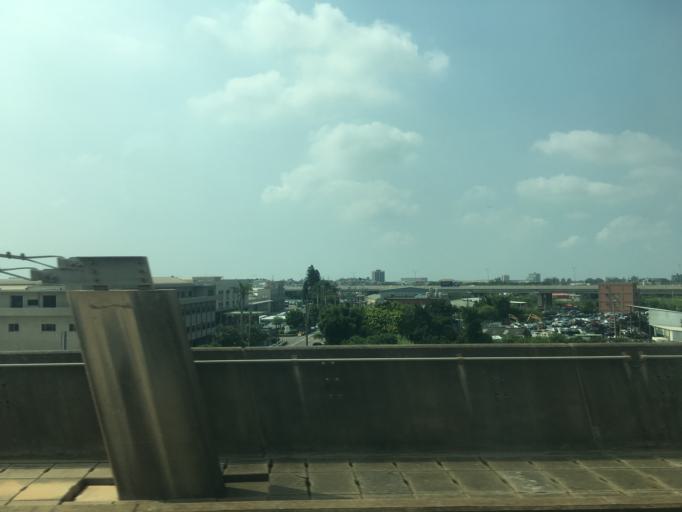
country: TW
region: Taiwan
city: Taoyuan City
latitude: 24.9546
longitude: 121.1478
